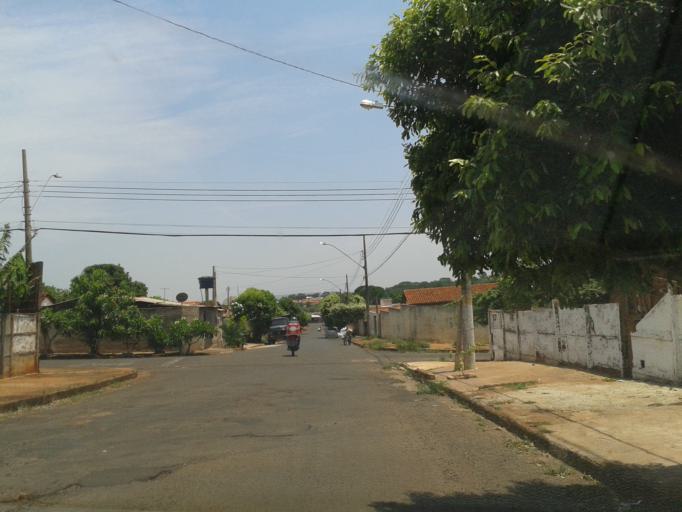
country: BR
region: Minas Gerais
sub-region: Ituiutaba
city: Ituiutaba
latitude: -18.9812
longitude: -49.4473
